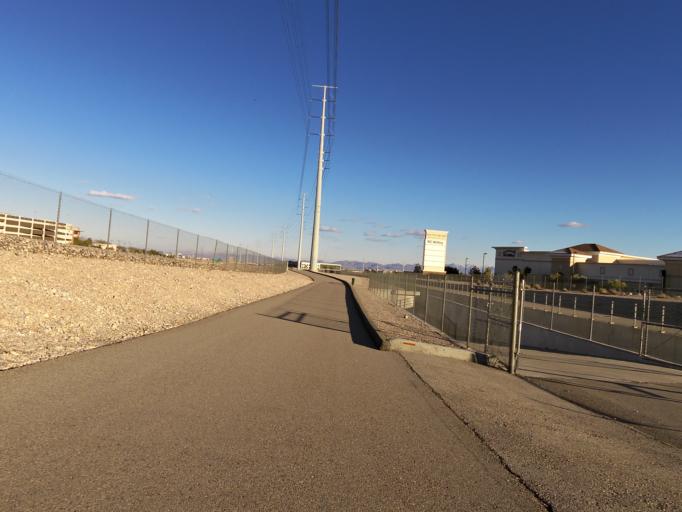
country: US
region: Nevada
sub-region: Clark County
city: Summerlin South
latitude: 36.1206
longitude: -115.3261
